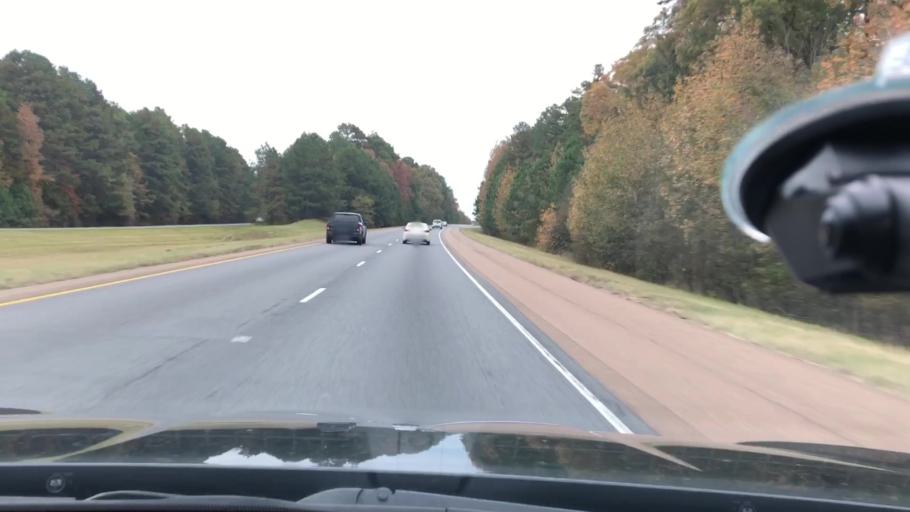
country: US
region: Arkansas
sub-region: Clark County
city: Gurdon
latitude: 33.9261
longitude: -93.2656
